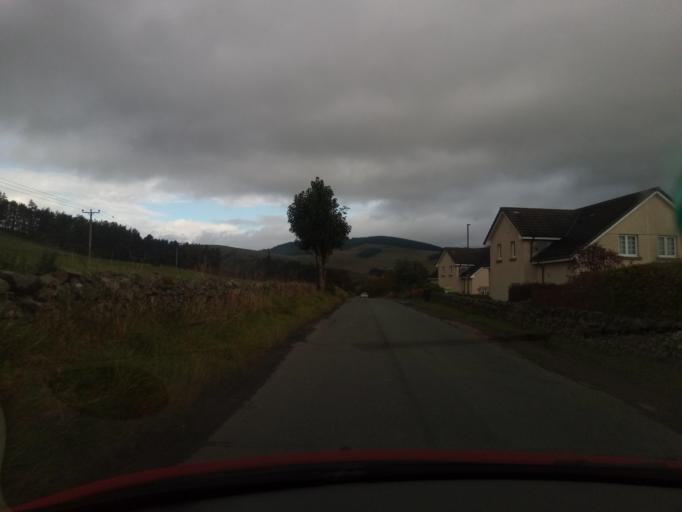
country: GB
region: Scotland
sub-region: The Scottish Borders
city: Innerleithen
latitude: 55.6348
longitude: -3.1065
